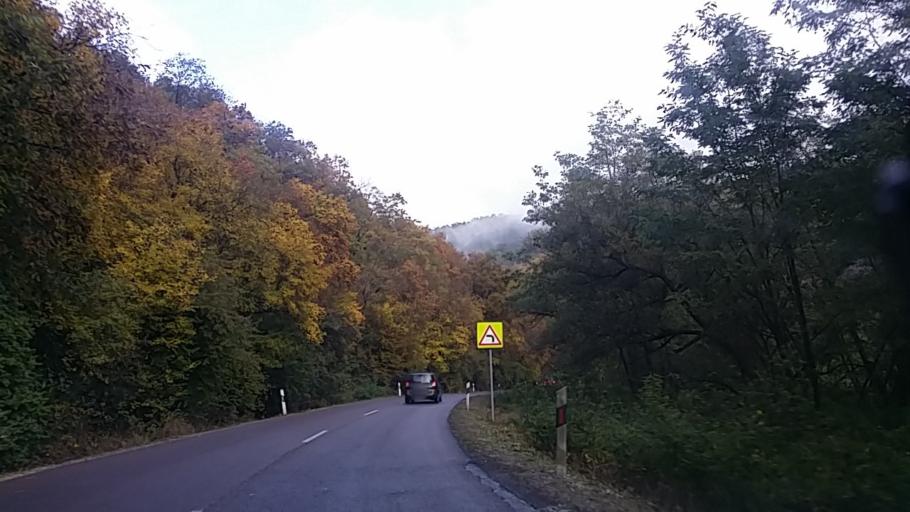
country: HU
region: Heves
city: Belapatfalva
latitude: 47.9848
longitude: 20.3433
